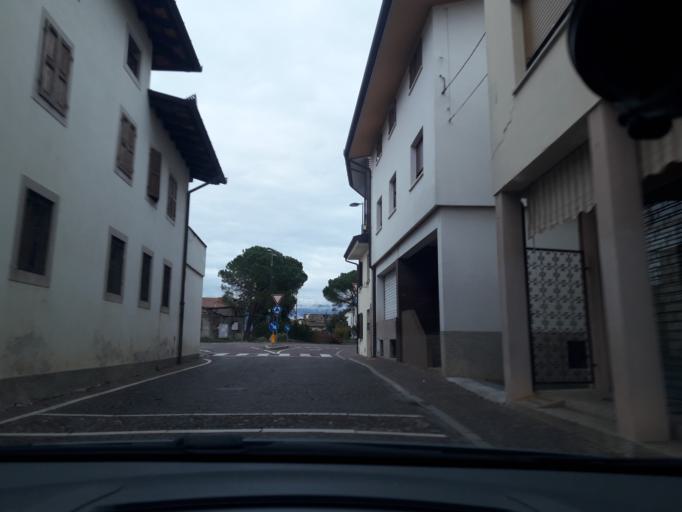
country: IT
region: Friuli Venezia Giulia
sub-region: Provincia di Udine
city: Tavagnacco
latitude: 46.1147
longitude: 13.2349
